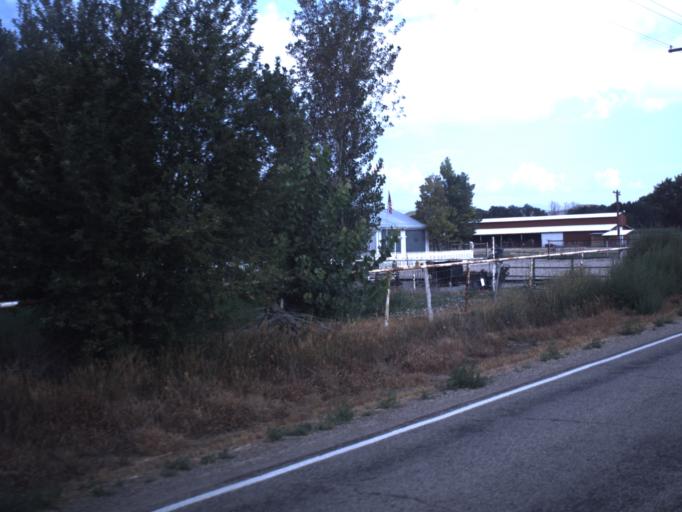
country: US
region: Utah
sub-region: Uintah County
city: Naples
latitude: 40.3819
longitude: -109.3458
